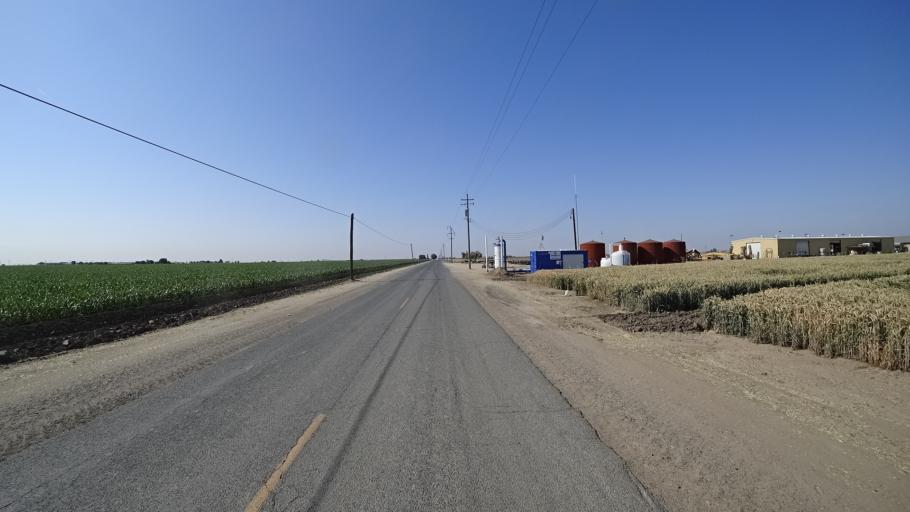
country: US
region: California
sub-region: Kings County
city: Home Garden
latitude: 36.2467
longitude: -119.5831
